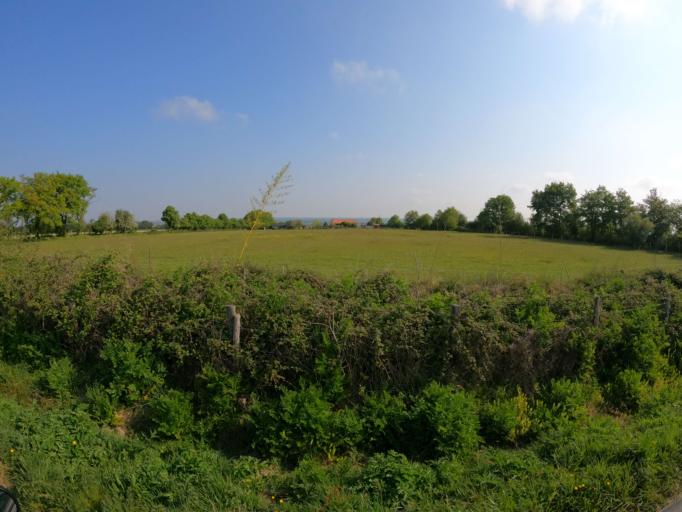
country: FR
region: Pays de la Loire
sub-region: Departement de Maine-et-Loire
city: La Romagne
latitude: 47.0646
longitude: -1.0418
